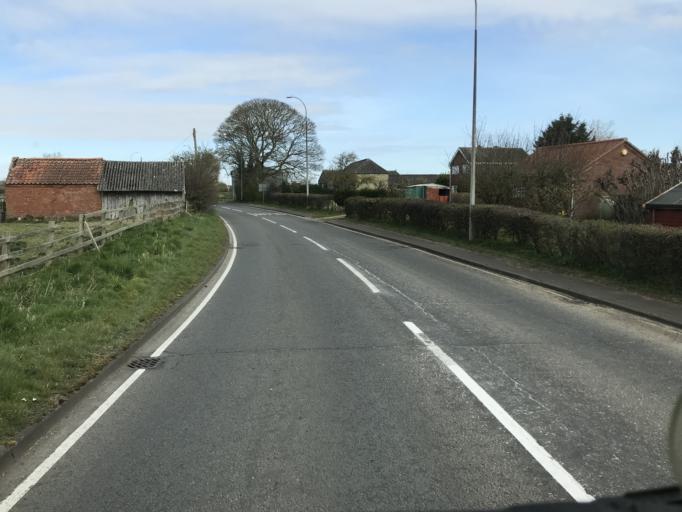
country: GB
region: England
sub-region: Lincolnshire
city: Market Rasen
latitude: 53.3898
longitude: -0.4043
